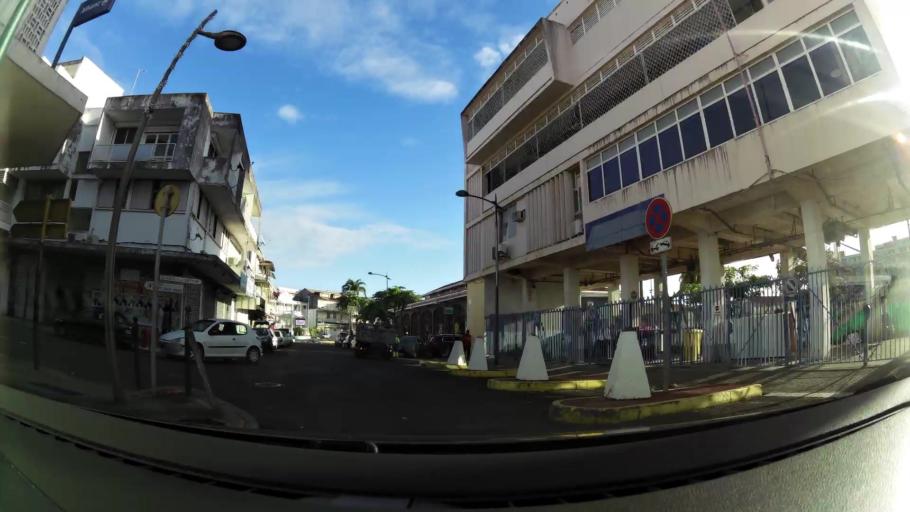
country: GP
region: Guadeloupe
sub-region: Guadeloupe
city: Pointe-a-Pitre
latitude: 16.2359
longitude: -61.5355
